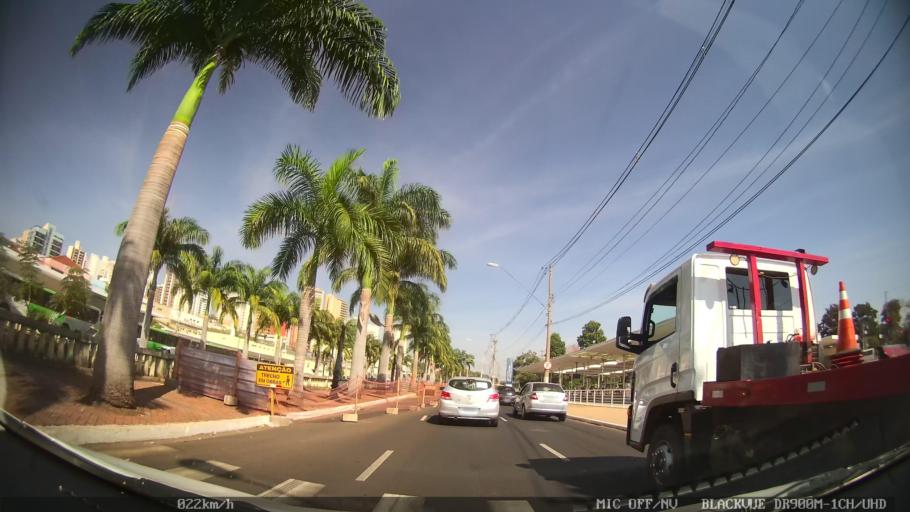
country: BR
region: Sao Paulo
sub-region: Ribeirao Preto
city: Ribeirao Preto
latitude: -21.1752
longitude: -47.8146
